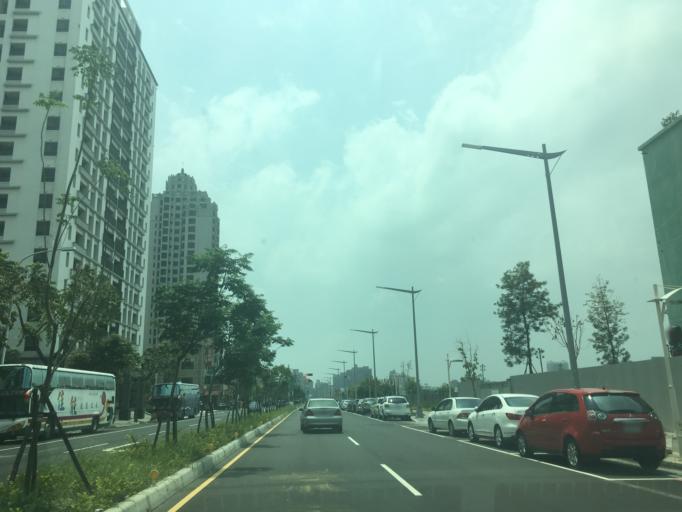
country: TW
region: Taiwan
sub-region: Taichung City
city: Taichung
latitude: 24.1880
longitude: 120.6824
